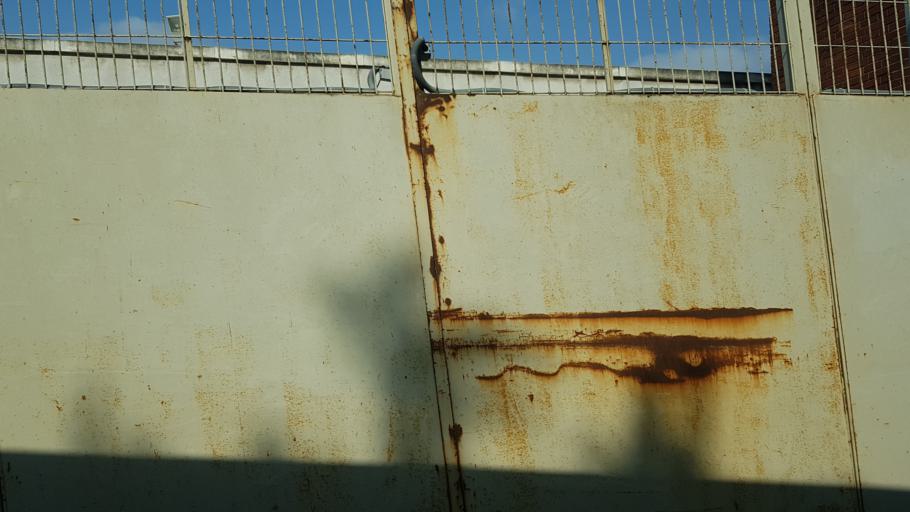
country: TR
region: Istanbul
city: Maltepe
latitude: 40.8991
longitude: 29.2018
